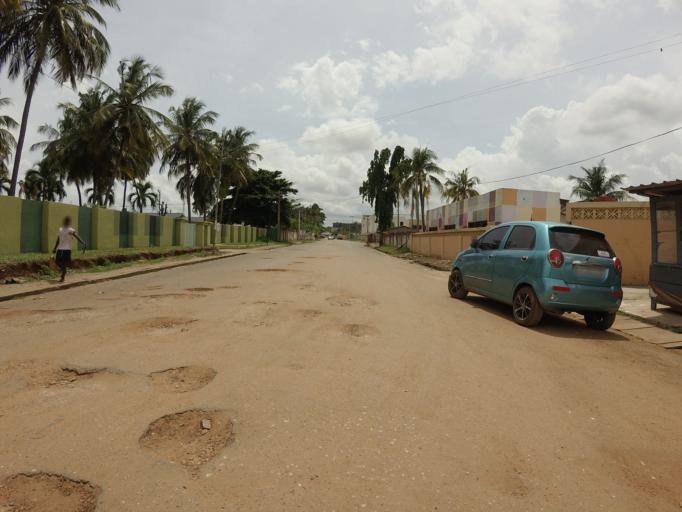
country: GH
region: Greater Accra
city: Accra
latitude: 5.6030
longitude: -0.2091
